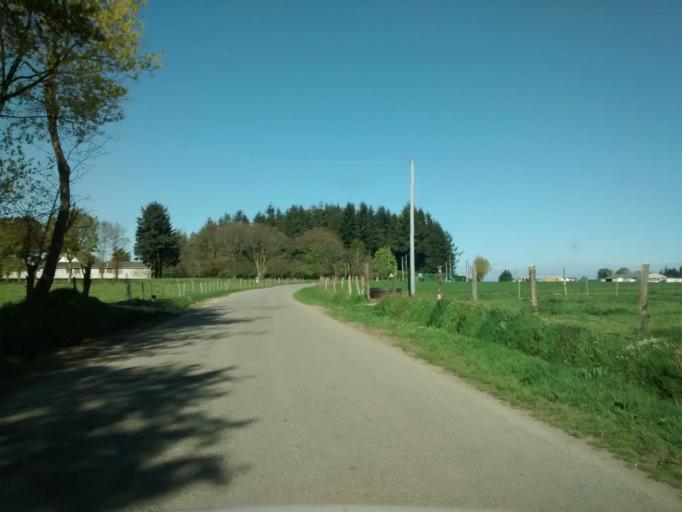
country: FR
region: Brittany
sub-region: Departement du Morbihan
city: Malestroit
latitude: 47.8615
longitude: -2.4124
